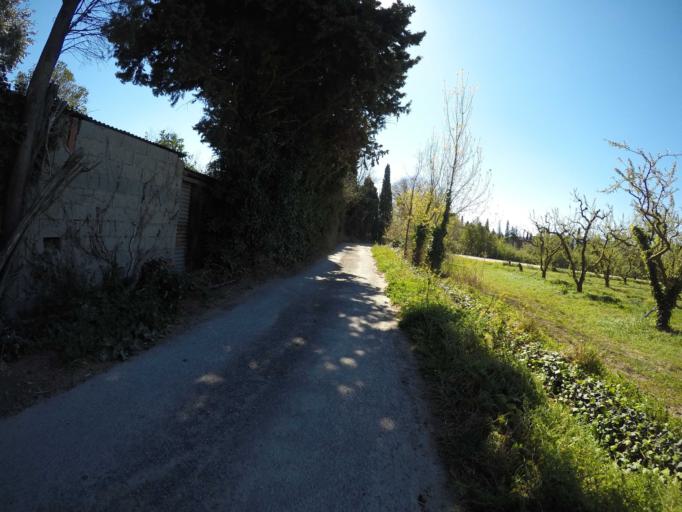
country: FR
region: Languedoc-Roussillon
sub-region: Departement des Pyrenees-Orientales
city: Ille-sur-Tet
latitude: 42.6846
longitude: 2.6551
